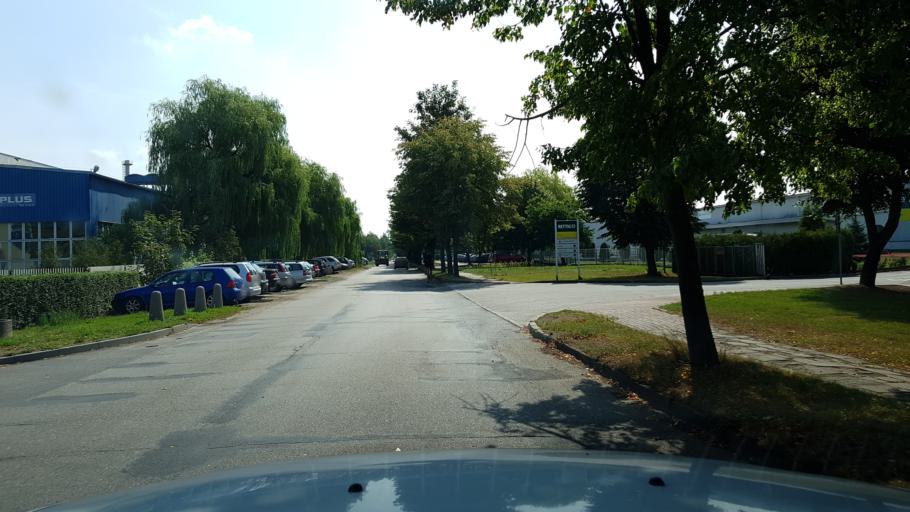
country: PL
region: West Pomeranian Voivodeship
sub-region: Powiat walecki
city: Walcz
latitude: 53.2740
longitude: 16.4898
